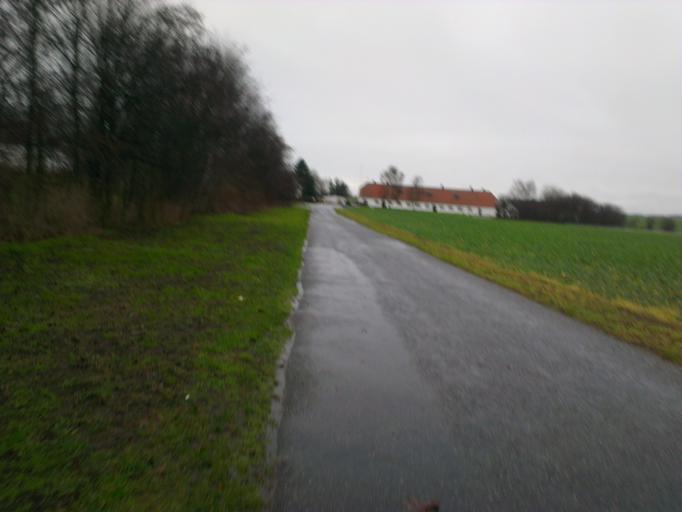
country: DK
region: Capital Region
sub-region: Frederikssund Kommune
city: Jaegerspris
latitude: 55.8309
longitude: 11.9990
